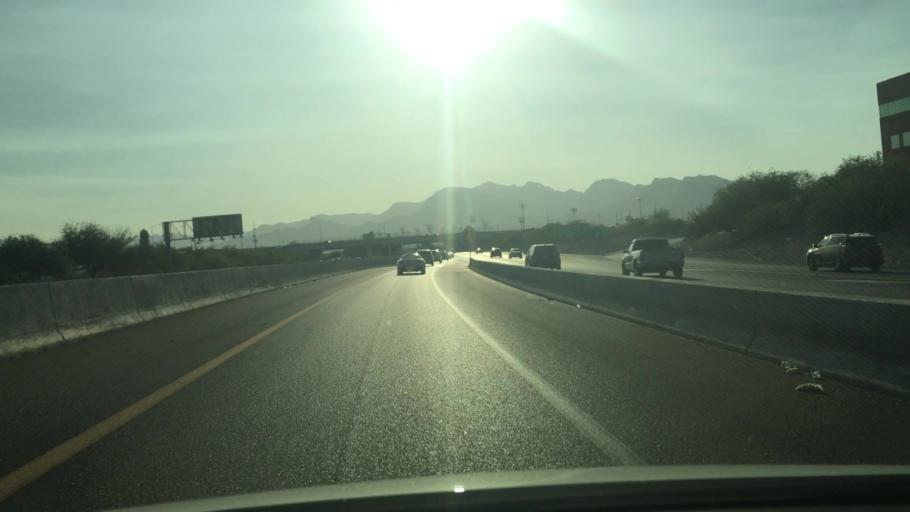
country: US
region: Nevada
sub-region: Clark County
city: Spring Valley
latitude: 36.1783
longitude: -115.2553
